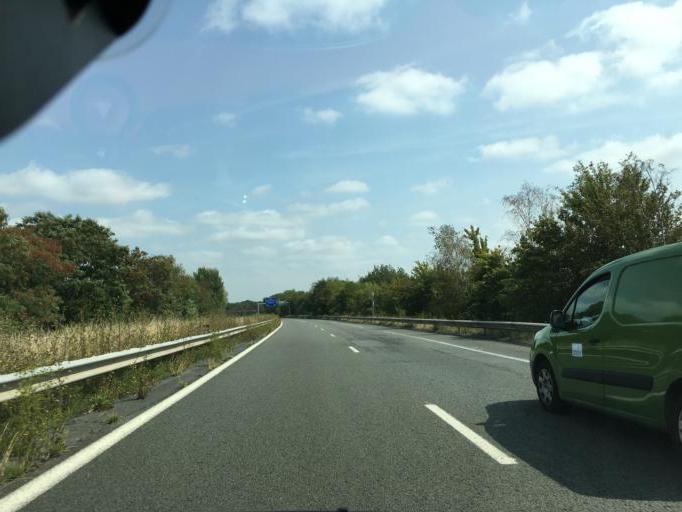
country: FR
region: Nord-Pas-de-Calais
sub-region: Departement du Nord
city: Lourches
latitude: 50.3226
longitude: 3.3534
